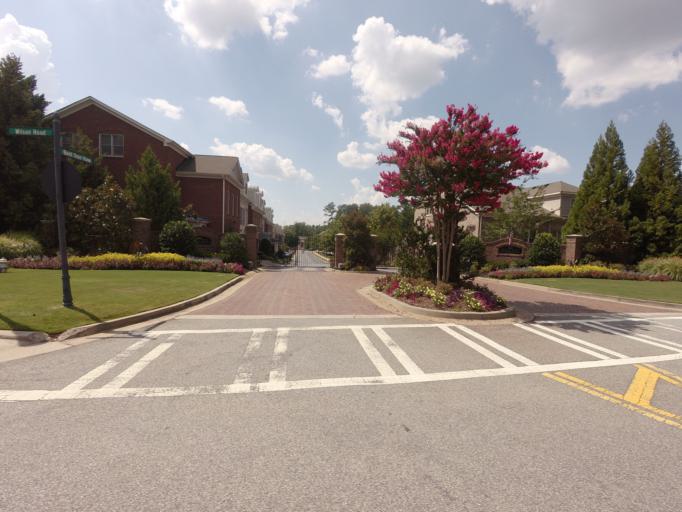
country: US
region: Georgia
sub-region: Fulton County
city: Johns Creek
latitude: 34.0360
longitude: -84.1805
